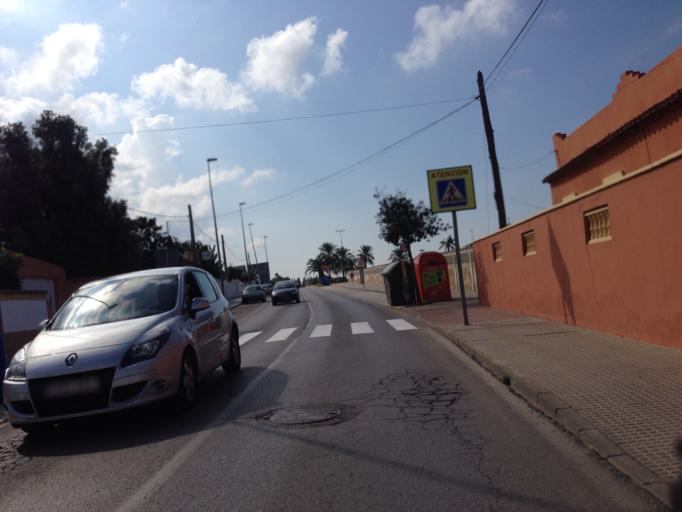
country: ES
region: Andalusia
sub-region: Provincia de Cadiz
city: Chiclana de la Frontera
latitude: 36.4086
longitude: -6.1664
